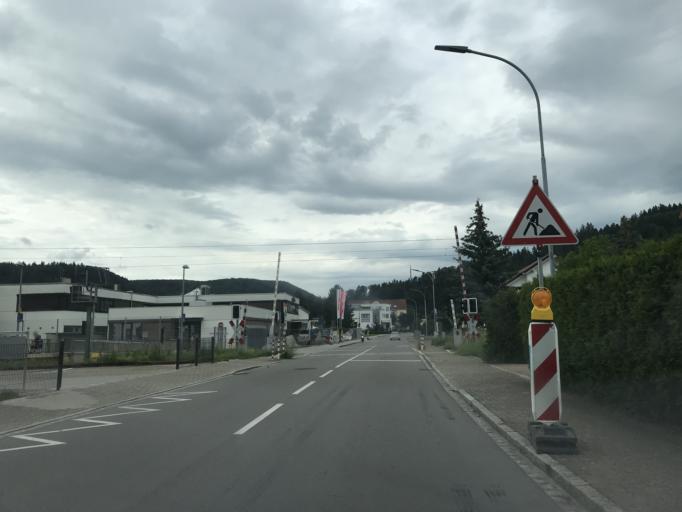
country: DE
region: Baden-Wuerttemberg
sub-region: Freiburg Region
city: Schopfheim
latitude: 47.6453
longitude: 7.8029
